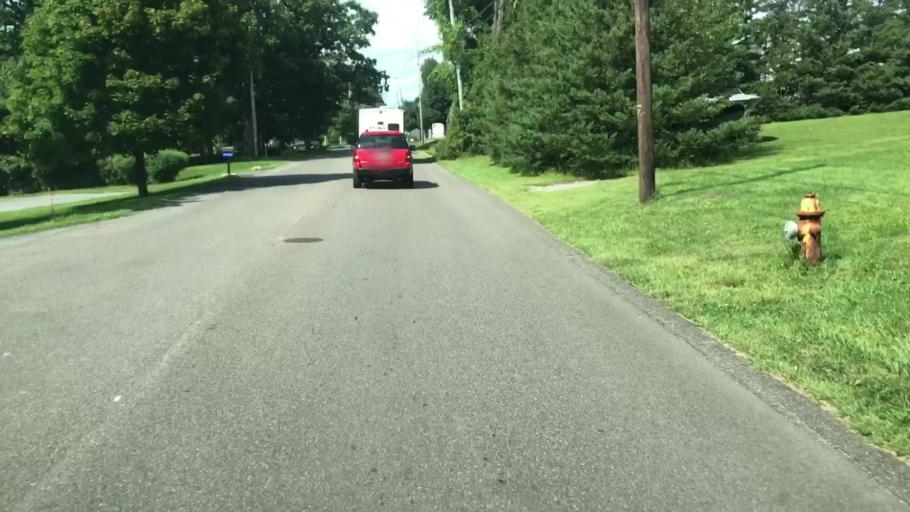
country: US
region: New York
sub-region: Cayuga County
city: Auburn
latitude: 42.9490
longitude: -76.5404
